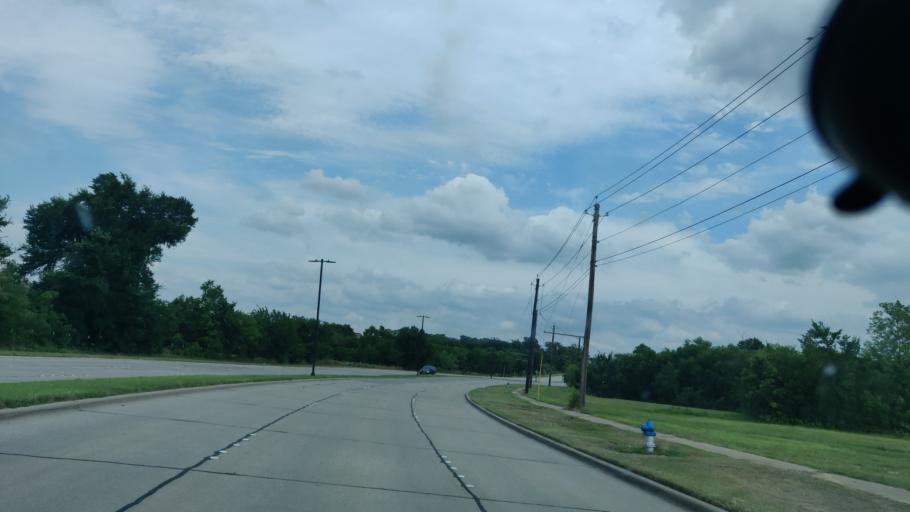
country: US
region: Texas
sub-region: Dallas County
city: Rowlett
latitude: 32.9310
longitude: -96.5895
